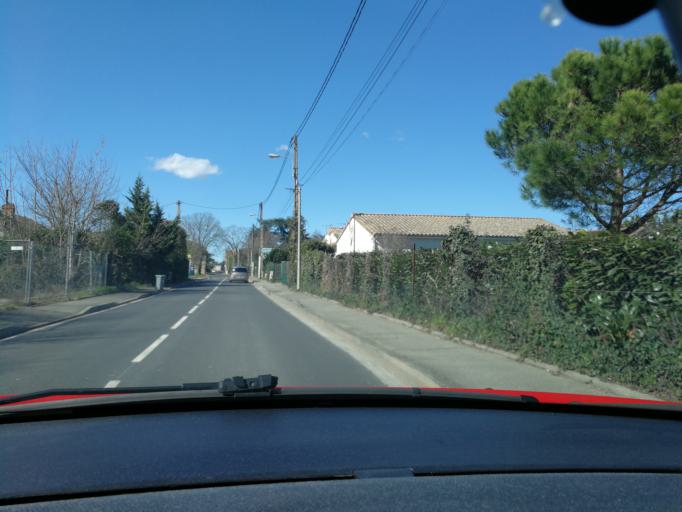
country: FR
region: Midi-Pyrenees
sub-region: Departement de la Haute-Garonne
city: Portet-sur-Garonne
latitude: 43.5506
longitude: 1.3800
